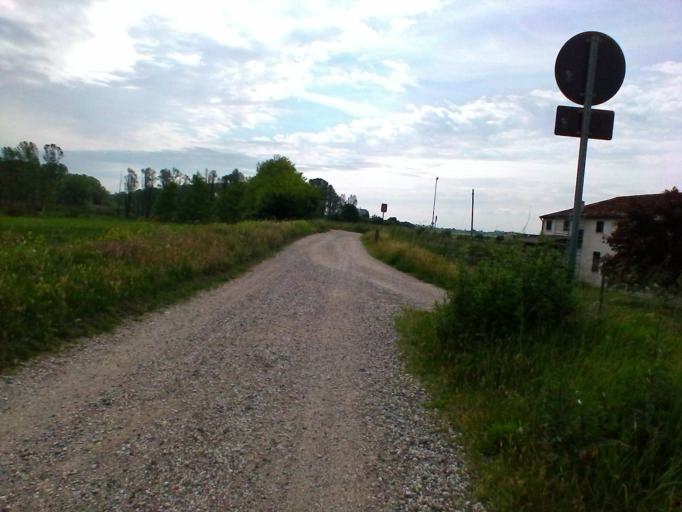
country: IT
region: Lombardy
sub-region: Provincia di Mantova
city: Lunetta-Frassino
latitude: 45.1286
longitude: 10.8234
